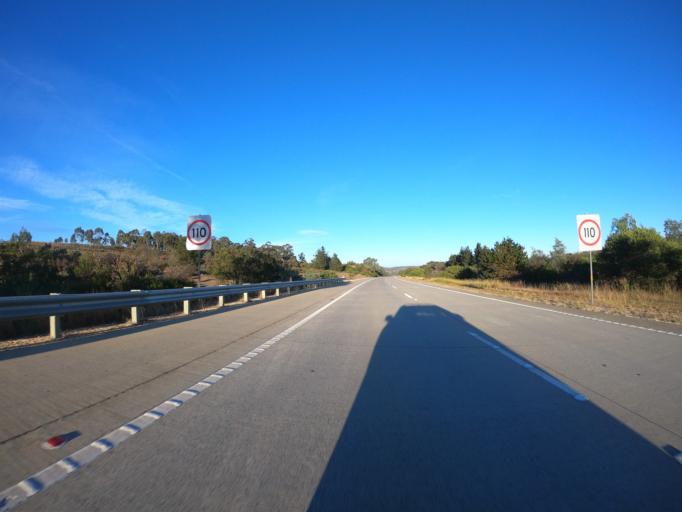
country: AU
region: New South Wales
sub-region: Yass Valley
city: Gundaroo
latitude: -35.1127
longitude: 149.3640
